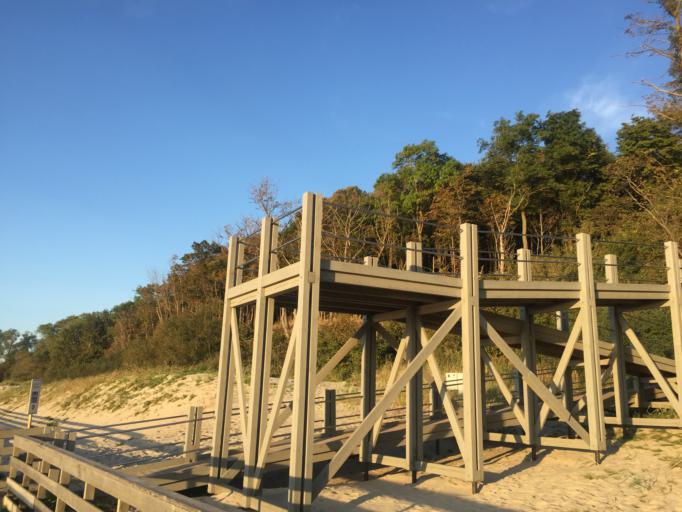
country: RU
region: Kaliningrad
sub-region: Gorod Kaliningrad
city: Yantarnyy
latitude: 54.8692
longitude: 19.9334
